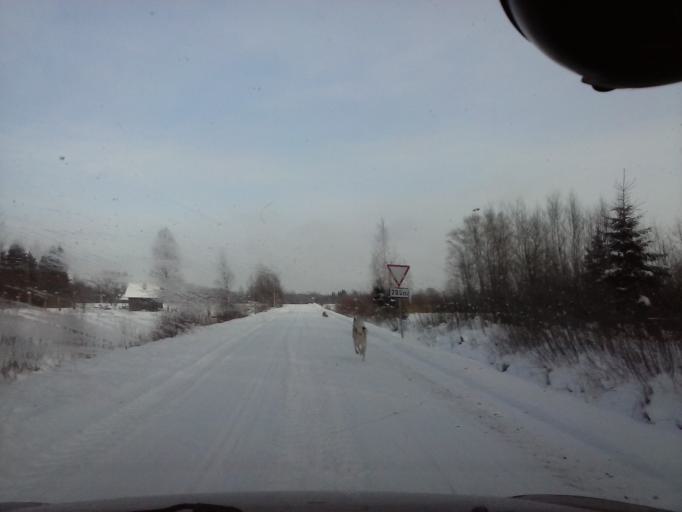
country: EE
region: Paernumaa
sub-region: Paikuse vald
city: Paikuse
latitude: 58.2021
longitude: 24.7228
